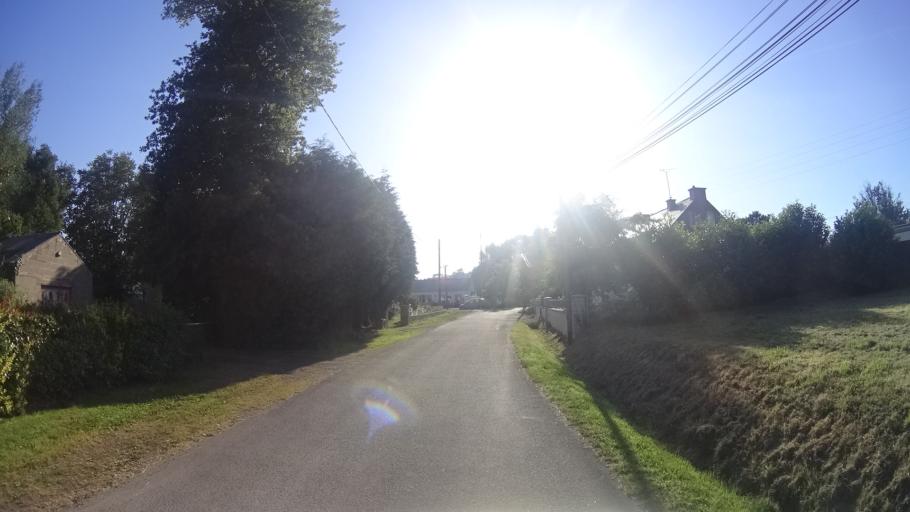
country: FR
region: Brittany
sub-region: Departement du Morbihan
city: Rieux
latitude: 47.6164
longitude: -2.1083
